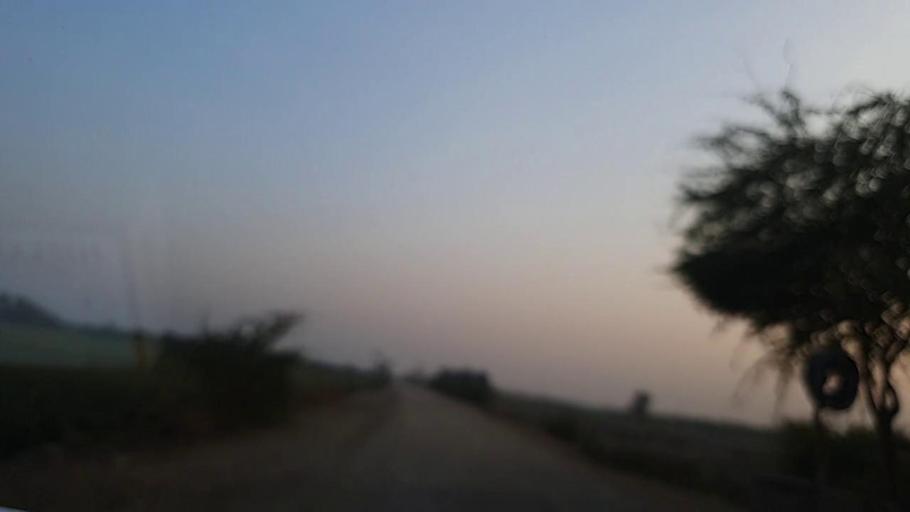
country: PK
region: Sindh
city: Tando Ghulam Ali
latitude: 25.1659
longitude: 68.9219
